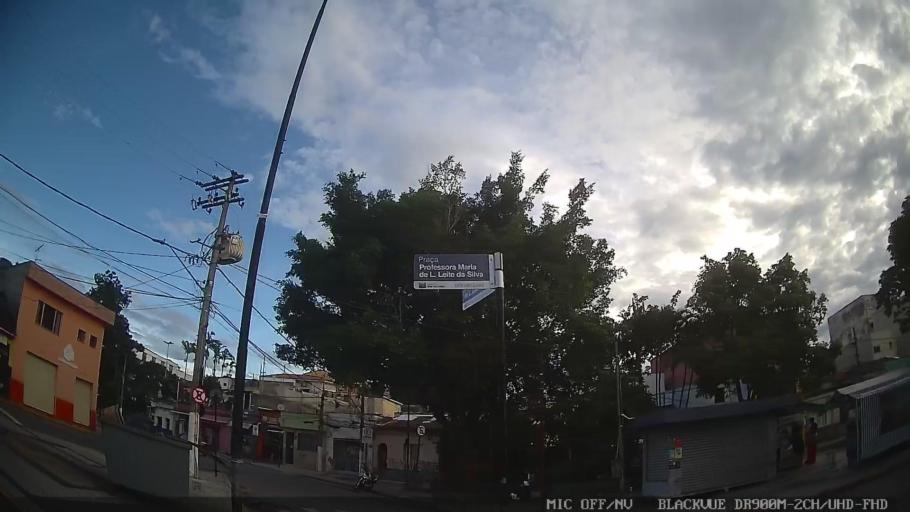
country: BR
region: Sao Paulo
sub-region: Mogi das Cruzes
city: Mogi das Cruzes
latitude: -23.5244
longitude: -46.1899
